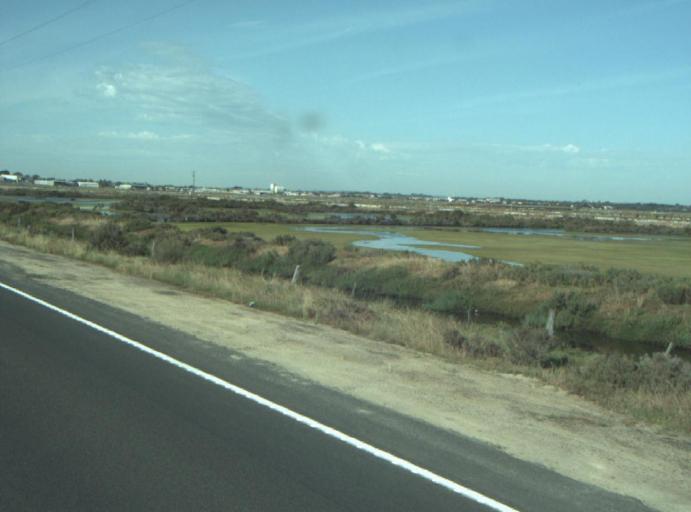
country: AU
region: Victoria
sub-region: Greater Geelong
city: Leopold
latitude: -38.1536
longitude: 144.4328
